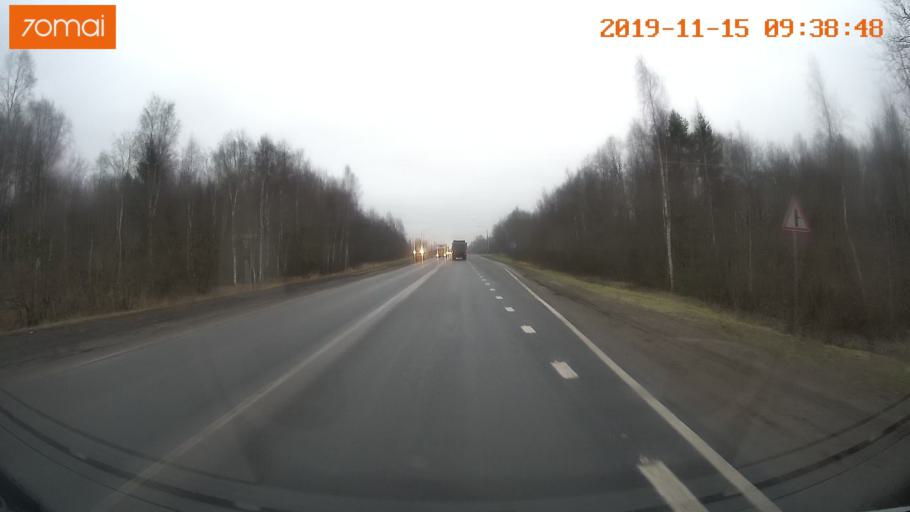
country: RU
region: Vologda
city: Sheksna
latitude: 59.2288
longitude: 38.4619
